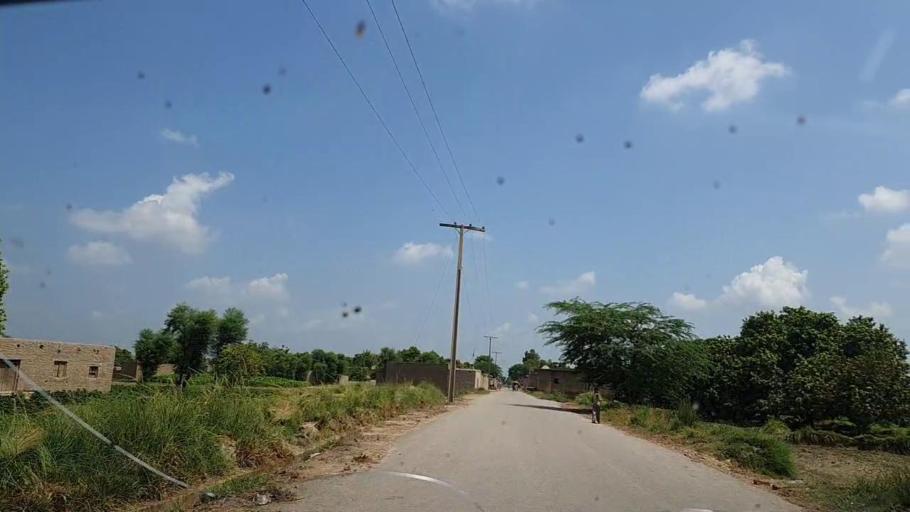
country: PK
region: Sindh
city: Tharu Shah
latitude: 26.9617
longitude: 68.0990
